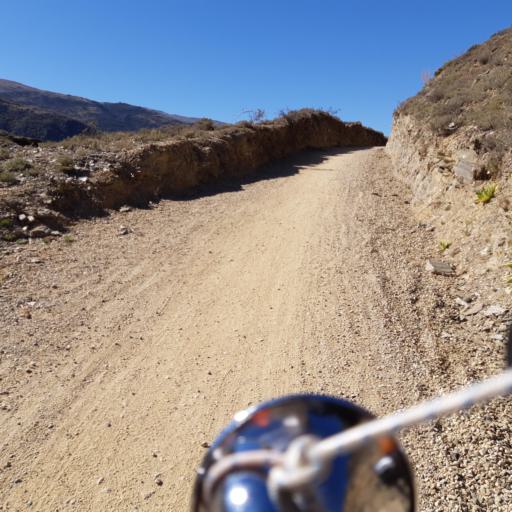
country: NZ
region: Otago
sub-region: Queenstown-Lakes District
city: Wanaka
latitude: -45.0851
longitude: 169.2517
